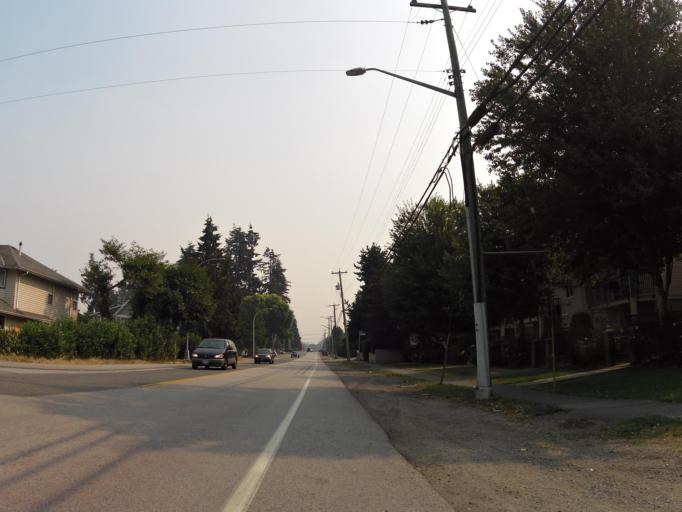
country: CA
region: British Columbia
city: Delta
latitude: 49.1559
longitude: -122.8864
